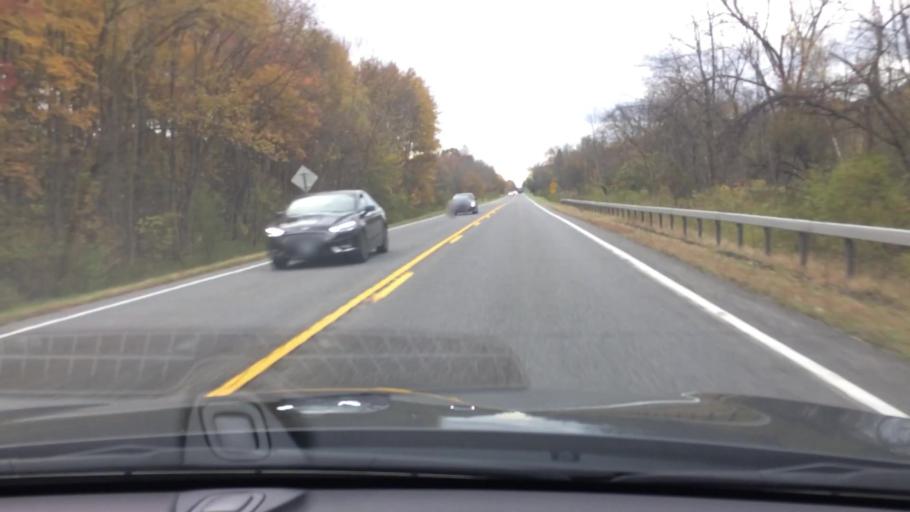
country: US
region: New York
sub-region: Columbia County
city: Kinderhook
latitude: 42.3639
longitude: -73.7055
